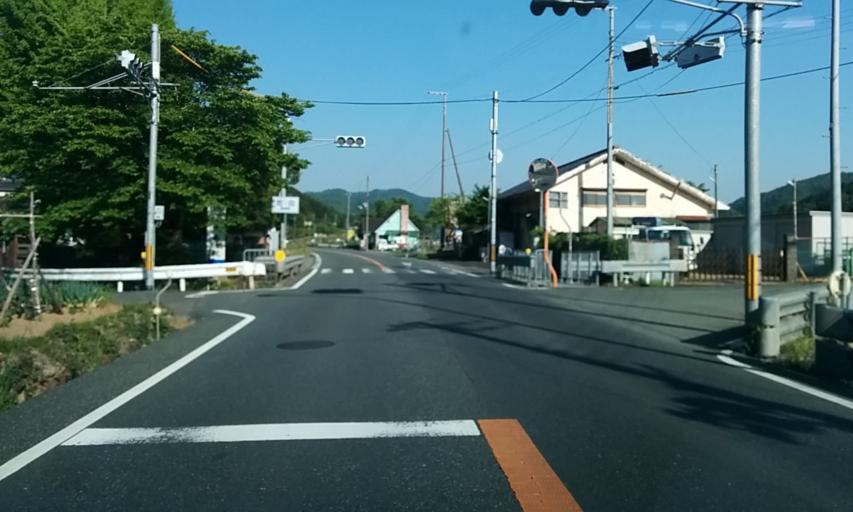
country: JP
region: Kyoto
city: Ayabe
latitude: 35.2593
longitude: 135.1953
